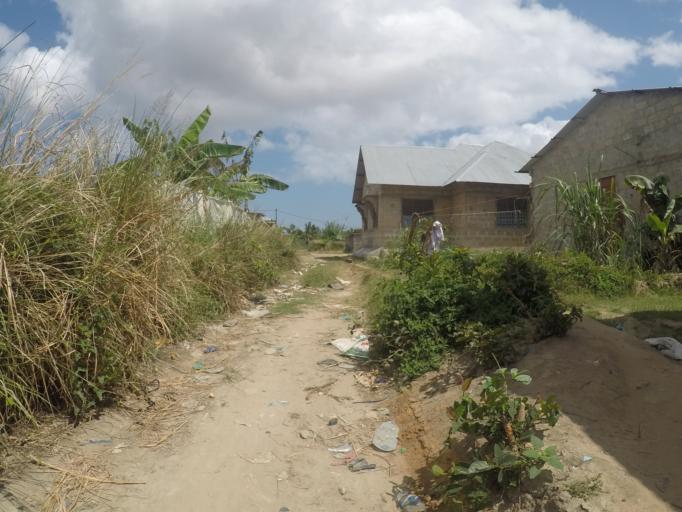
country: TZ
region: Zanzibar Urban/West
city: Zanzibar
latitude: -6.2007
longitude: 39.2382
